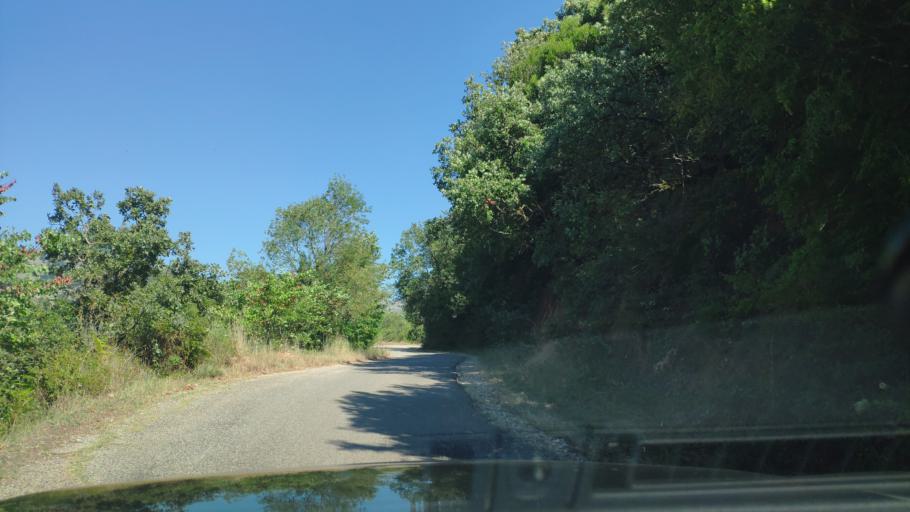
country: GR
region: West Greece
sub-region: Nomos Aitolias kai Akarnanias
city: Katouna
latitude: 38.8358
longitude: 21.0983
